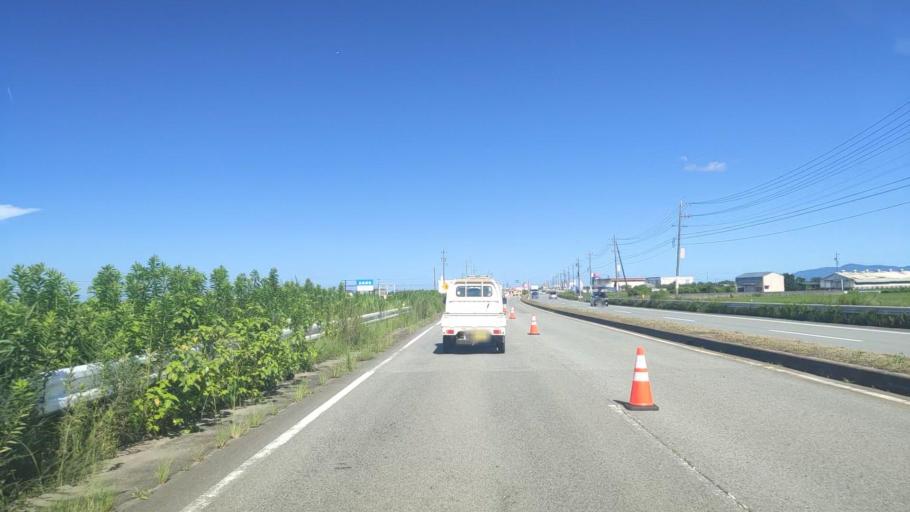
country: JP
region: Mie
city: Ise
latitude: 34.5870
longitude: 136.5993
